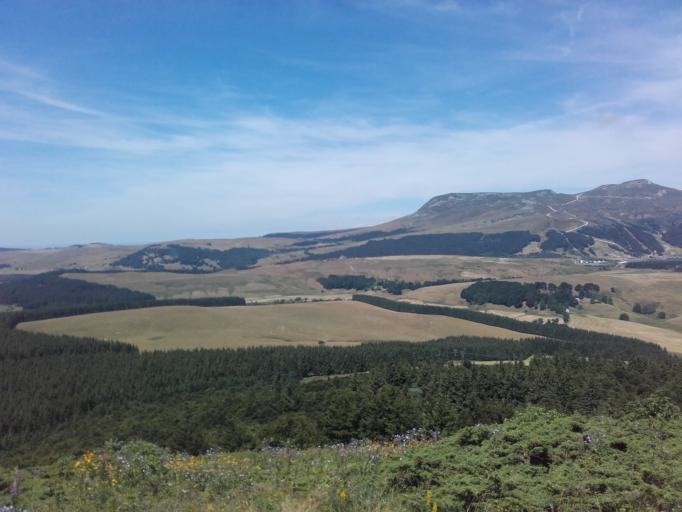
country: FR
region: Auvergne
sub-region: Departement du Puy-de-Dome
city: Mont-Dore
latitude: 45.4879
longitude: 2.8835
